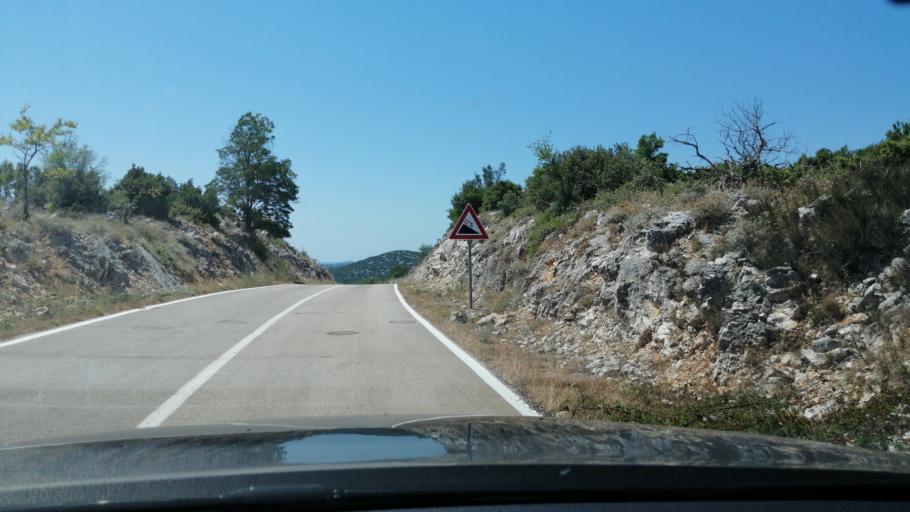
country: HR
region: Sibensko-Kniniska
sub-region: Grad Sibenik
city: Pirovac
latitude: 43.8571
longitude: 15.6922
